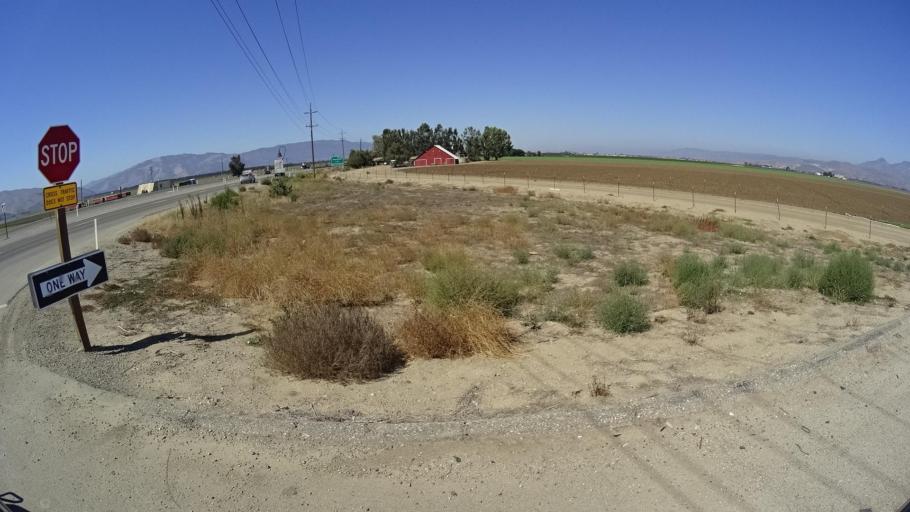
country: US
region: California
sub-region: Monterey County
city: Greenfield
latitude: 36.2967
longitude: -121.2167
